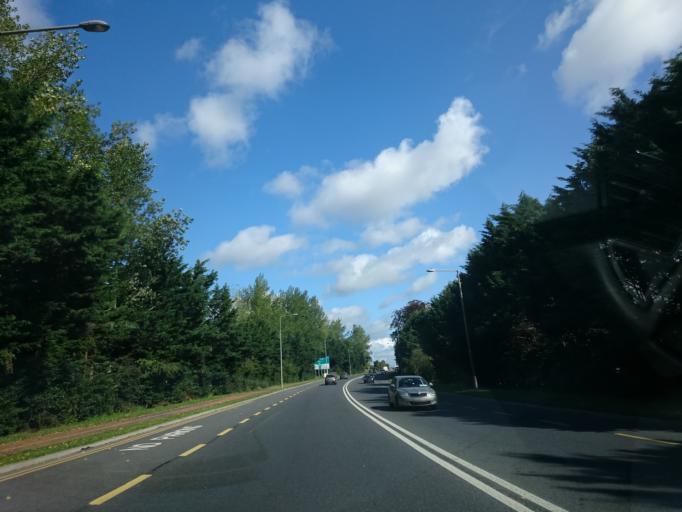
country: IE
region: Leinster
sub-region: Kilkenny
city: Kilkenny
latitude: 52.6460
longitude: -7.2305
